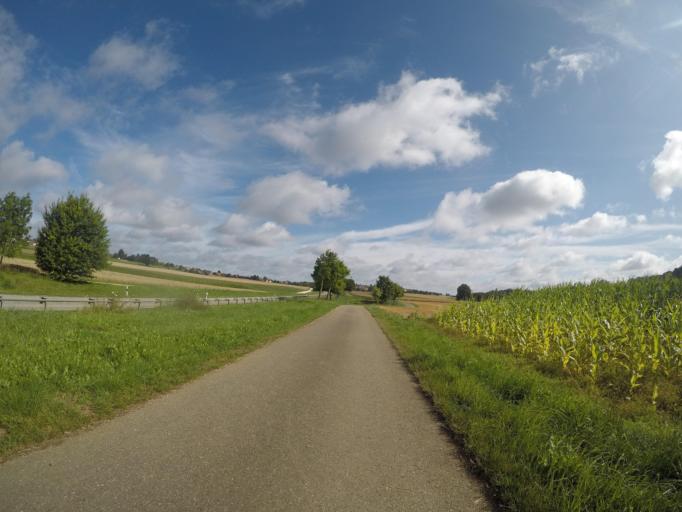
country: DE
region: Baden-Wuerttemberg
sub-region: Tuebingen Region
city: Laichingen
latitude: 48.4314
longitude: 9.6549
